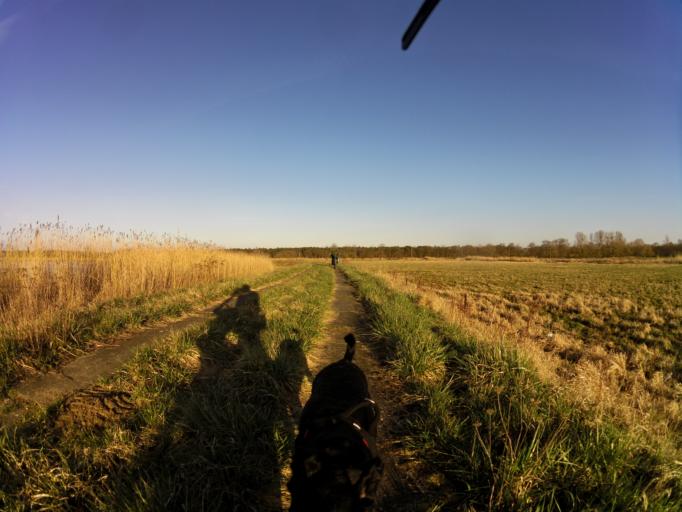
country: PL
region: West Pomeranian Voivodeship
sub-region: Powiat policki
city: Nowe Warpno
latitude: 53.7257
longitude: 14.2996
